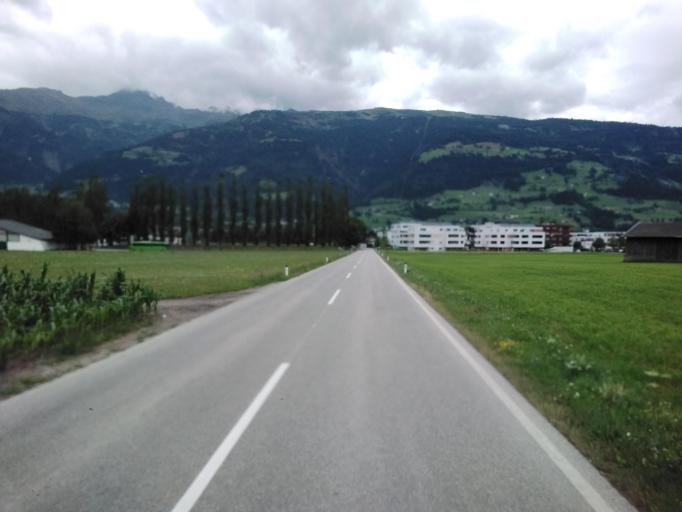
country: AT
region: Tyrol
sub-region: Politischer Bezirk Lienz
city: Amlach
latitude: 46.8209
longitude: 12.7673
